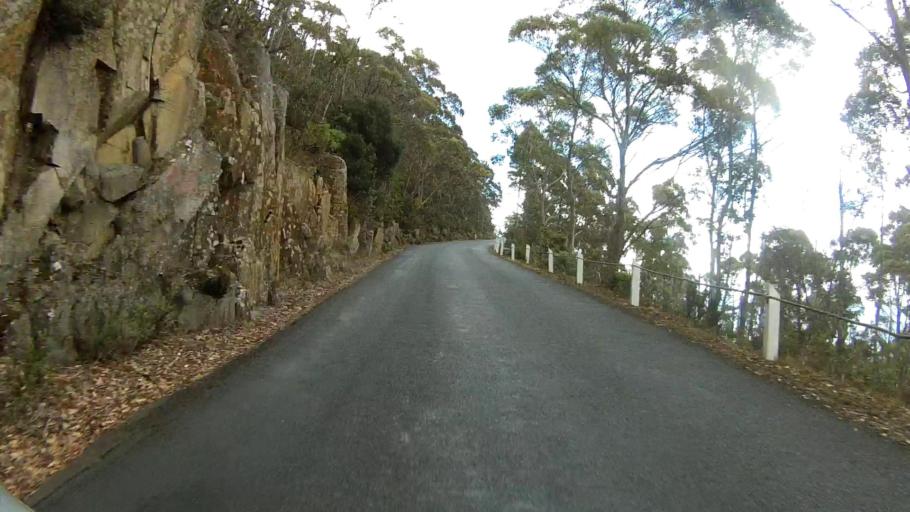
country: AU
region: Tasmania
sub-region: Glenorchy
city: West Moonah
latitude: -42.8930
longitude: 147.2441
